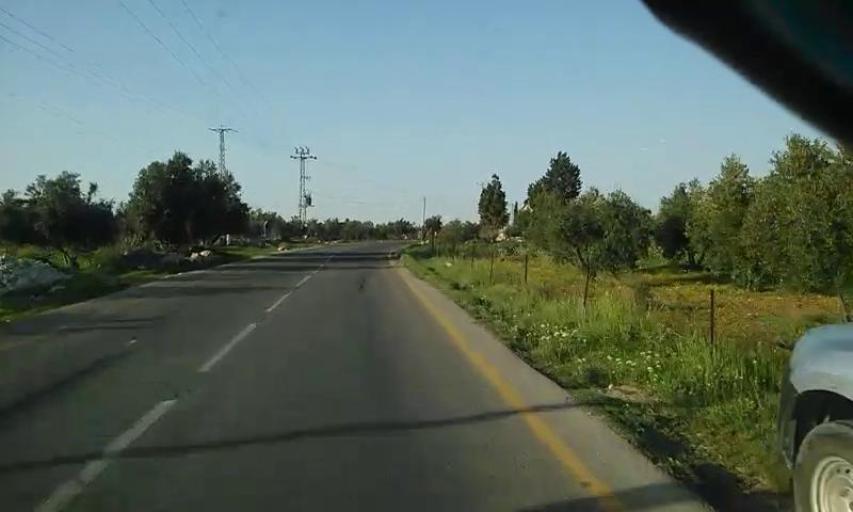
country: PS
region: West Bank
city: Marah Rabbah
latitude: 31.6457
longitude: 35.2023
